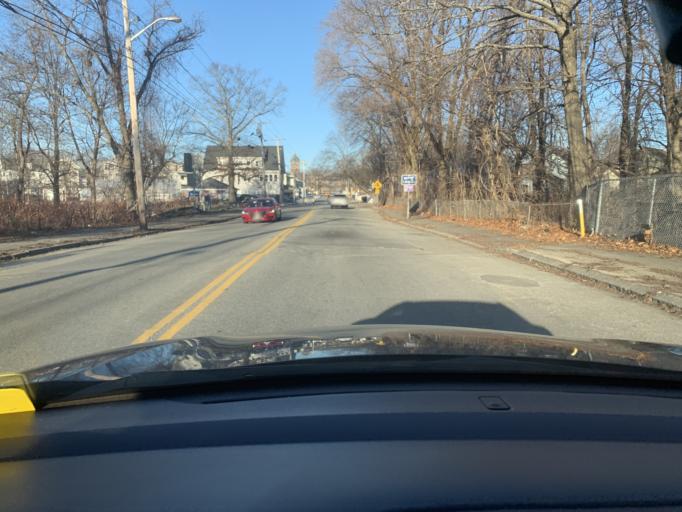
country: US
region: Massachusetts
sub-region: Essex County
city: North Andover
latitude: 42.6990
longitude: -71.1449
